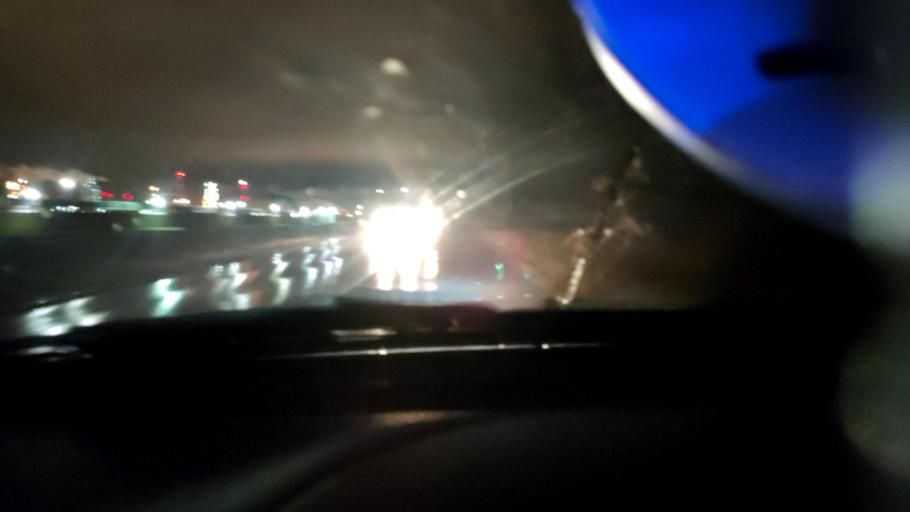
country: RU
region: Perm
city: Gamovo
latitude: 57.9146
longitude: 56.1114
